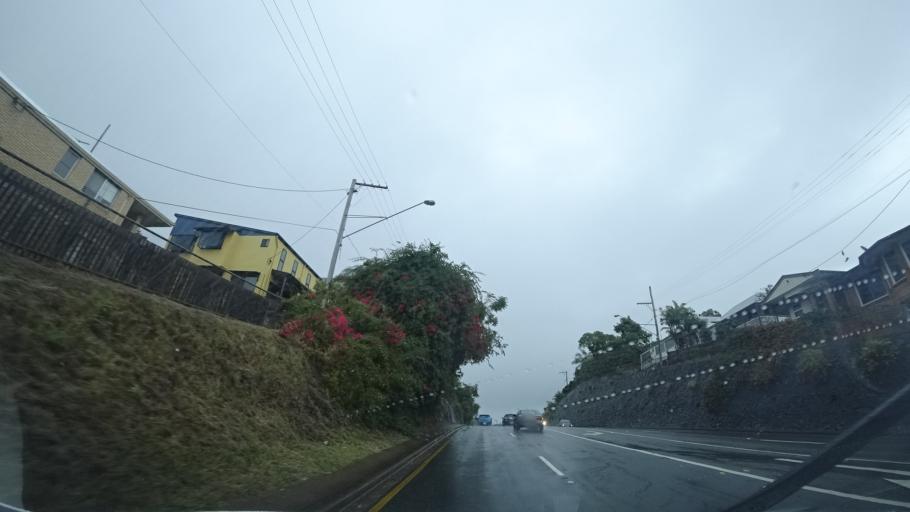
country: AU
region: Queensland
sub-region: Brisbane
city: Milton
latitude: -27.4745
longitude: 152.9948
